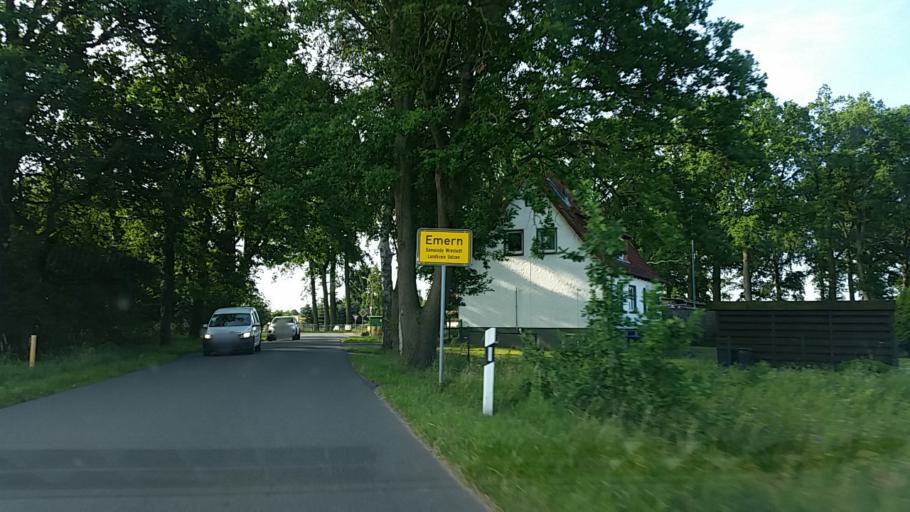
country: DE
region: Lower Saxony
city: Wieren
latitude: 52.9118
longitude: 10.6595
